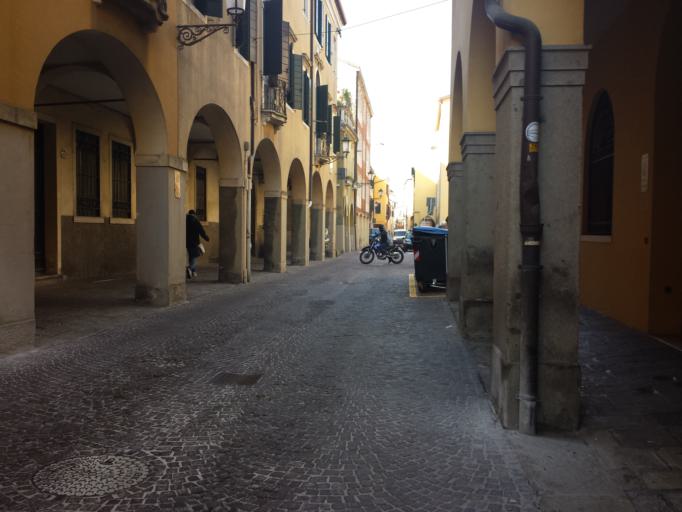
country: IT
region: Veneto
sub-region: Provincia di Padova
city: Padova
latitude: 45.4040
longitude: 11.8840
